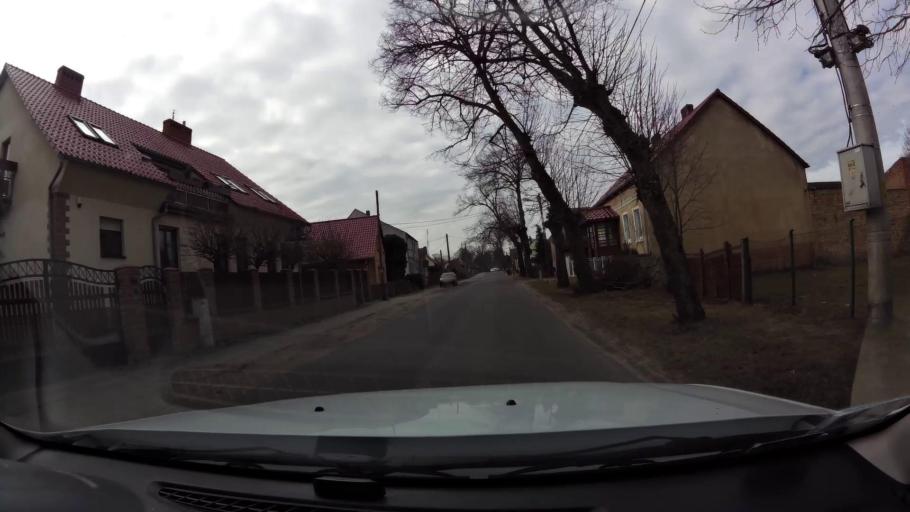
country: PL
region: West Pomeranian Voivodeship
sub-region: Powiat mysliborski
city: Debno
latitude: 52.7107
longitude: 14.6529
